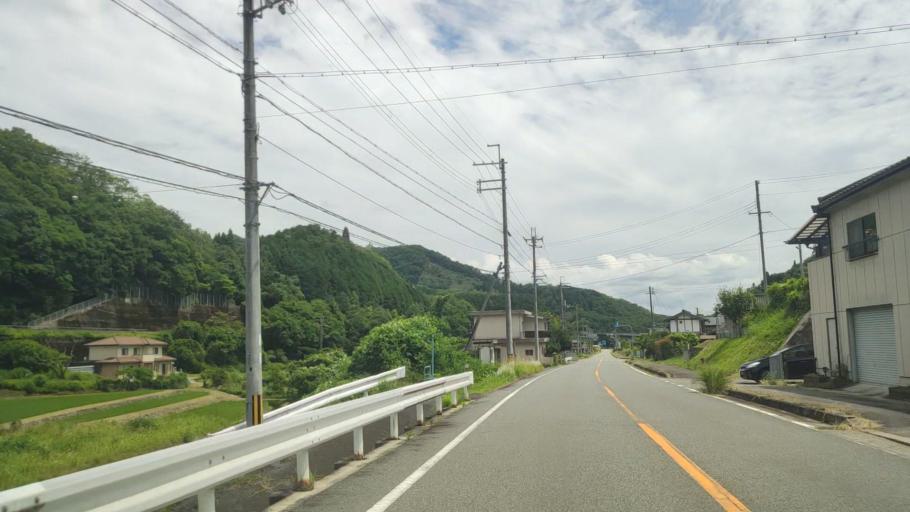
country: JP
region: Hyogo
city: Yamazakicho-nakabirose
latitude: 35.0634
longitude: 134.3639
